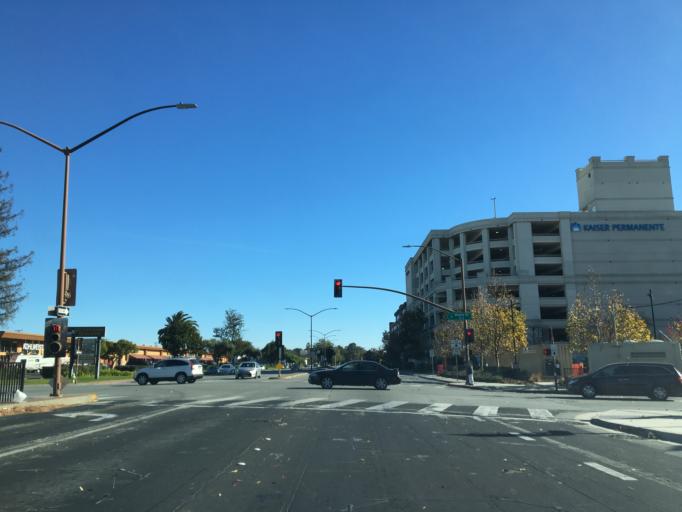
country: US
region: California
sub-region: San Mateo County
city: Redwood City
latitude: 37.4894
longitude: -122.2223
